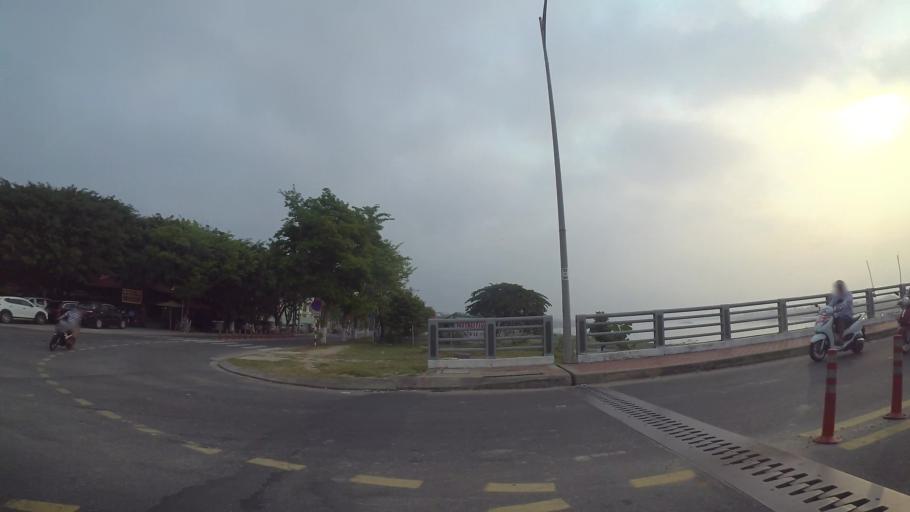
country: VN
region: Da Nang
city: Cam Le
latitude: 16.0251
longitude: 108.2220
